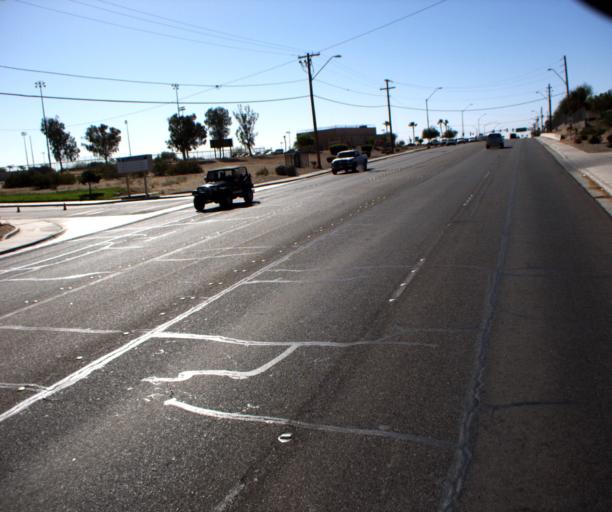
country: US
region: Arizona
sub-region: Yuma County
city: San Luis
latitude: 32.4972
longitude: -114.7851
